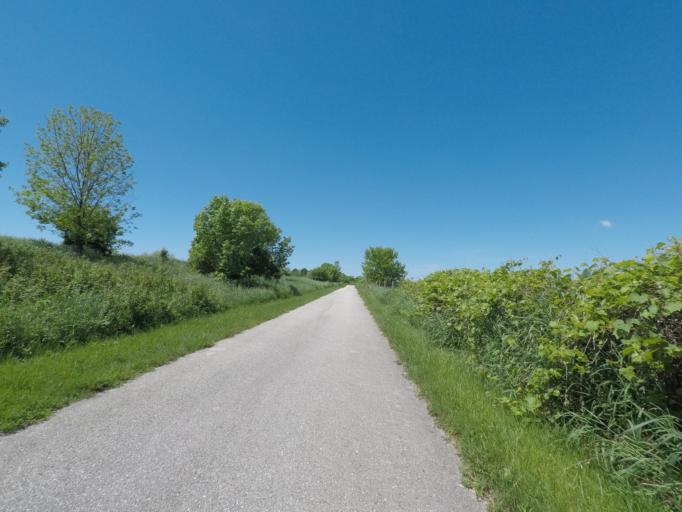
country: US
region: Wisconsin
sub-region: Sheboygan County
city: Kohler
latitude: 43.7517
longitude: -87.7930
